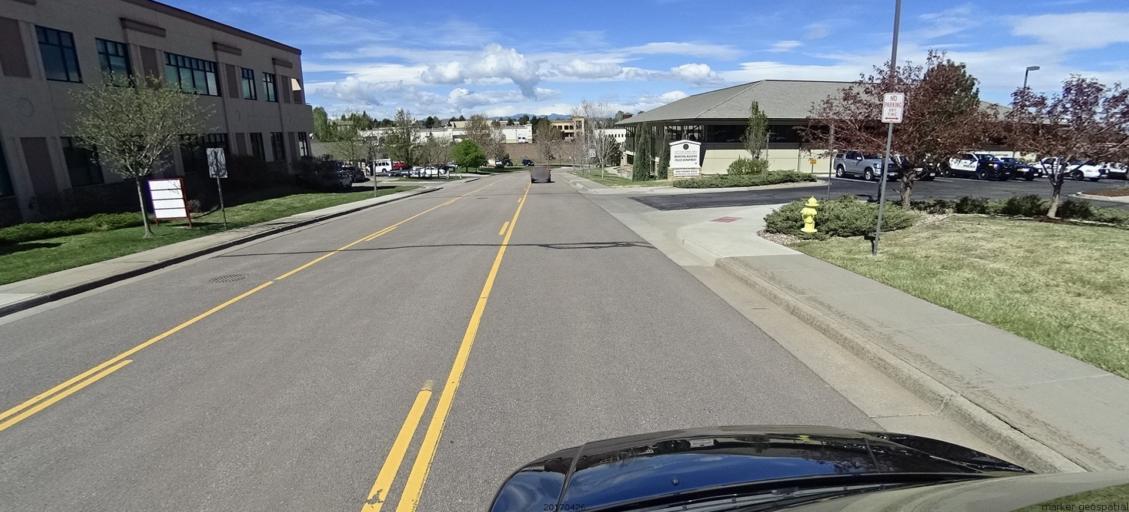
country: US
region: Colorado
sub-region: Adams County
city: Lone Tree
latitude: 39.5517
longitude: -104.8814
